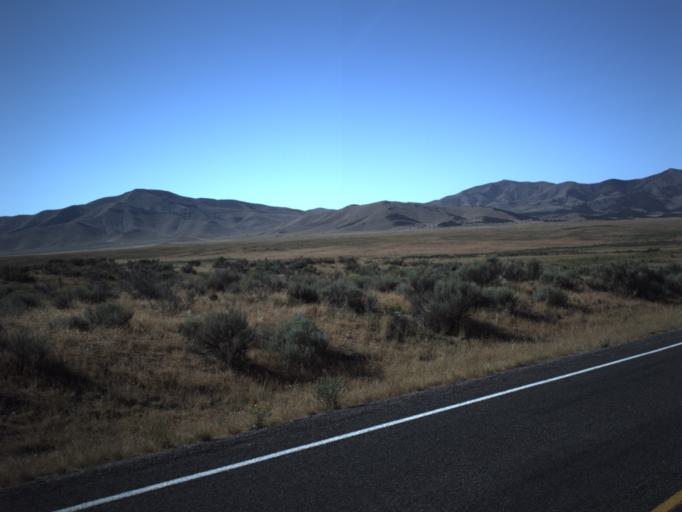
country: US
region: Utah
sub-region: Juab County
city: Mona
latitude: 39.7122
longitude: -112.2043
